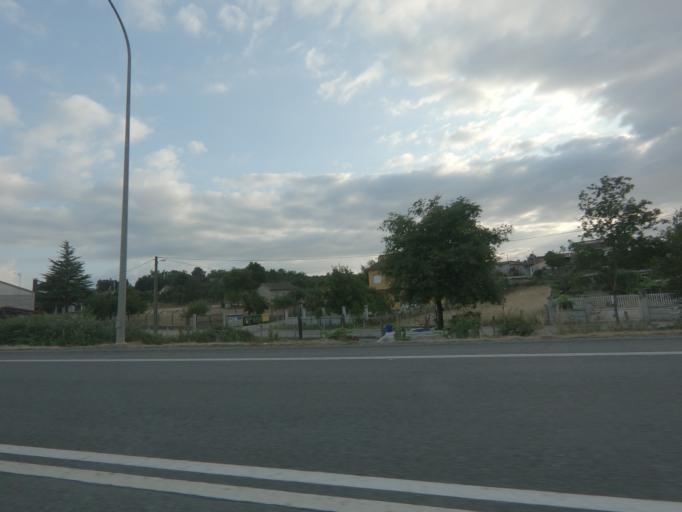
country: ES
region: Galicia
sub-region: Provincia de Ourense
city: Taboadela
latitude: 42.2822
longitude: -7.8396
